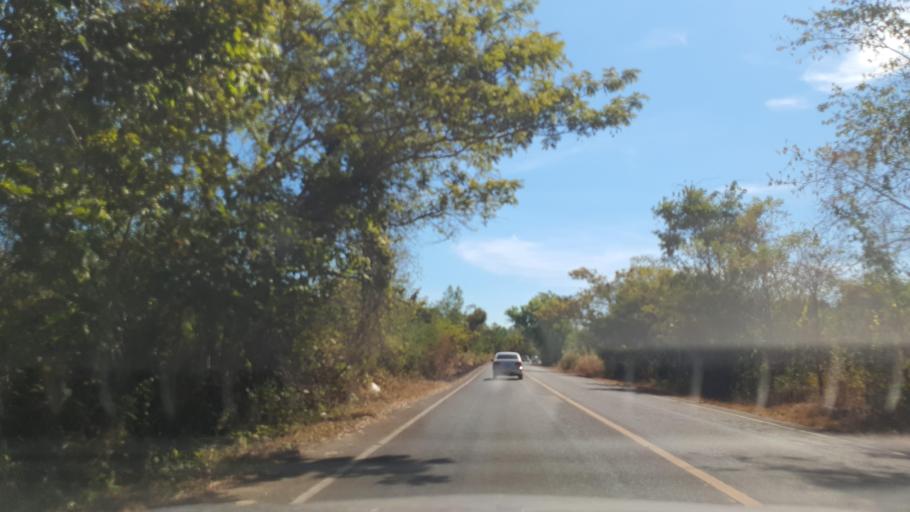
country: TH
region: Kalasin
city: Khao Wong
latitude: 16.8098
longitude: 104.1375
